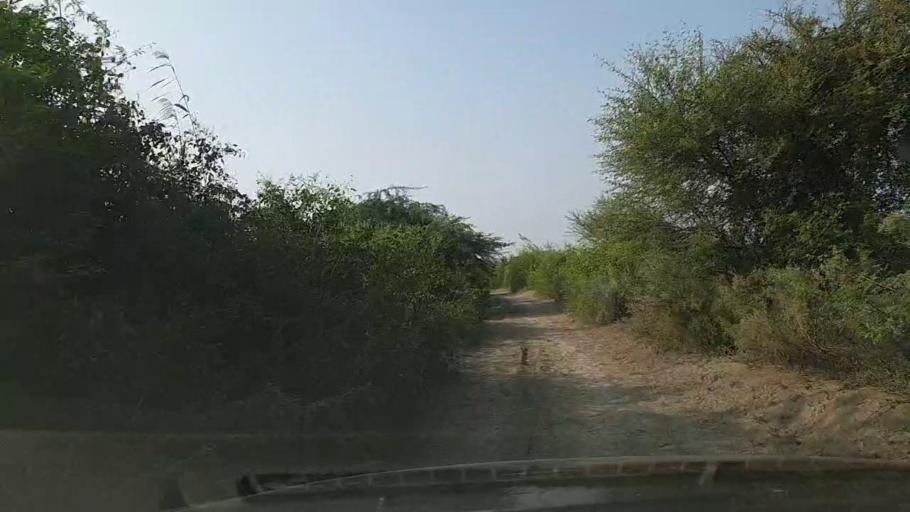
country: PK
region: Sindh
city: Mirpur Batoro
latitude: 24.6476
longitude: 68.2786
